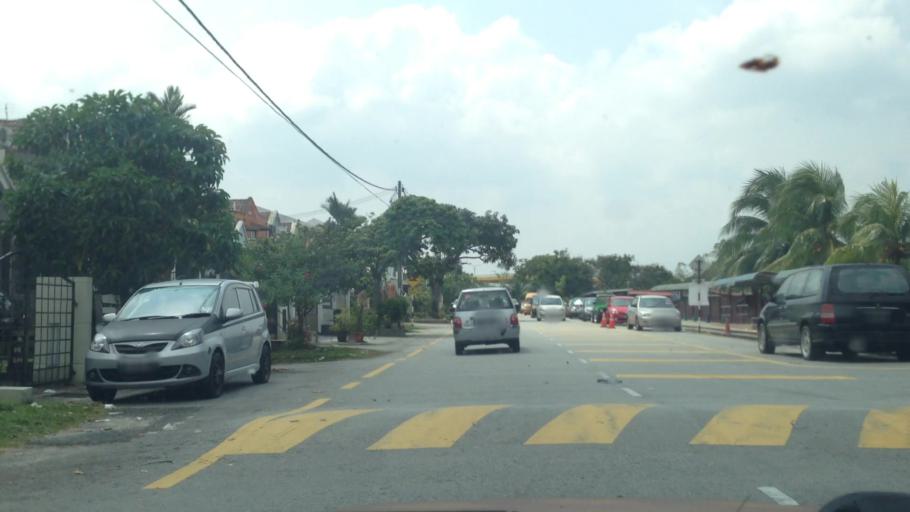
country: MY
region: Selangor
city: Subang Jaya
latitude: 3.0564
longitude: 101.5752
